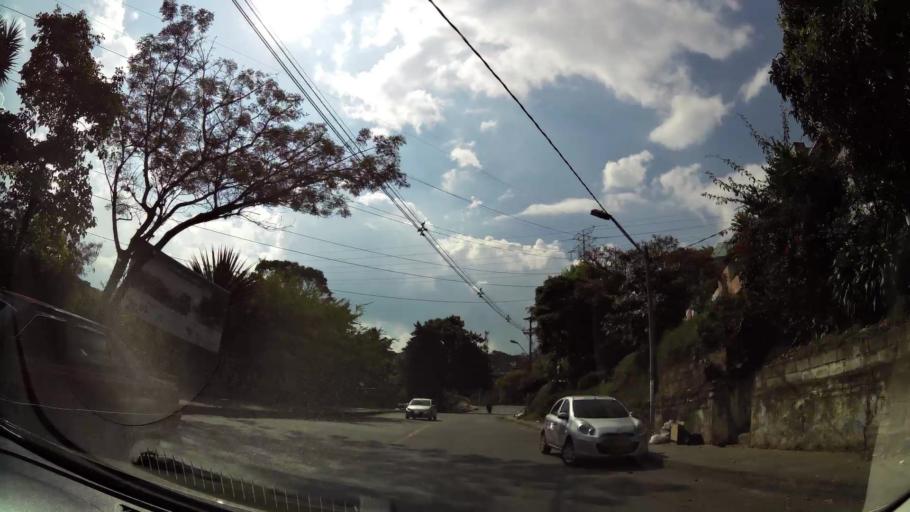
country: CO
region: Antioquia
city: Medellin
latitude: 6.2890
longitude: -75.5910
